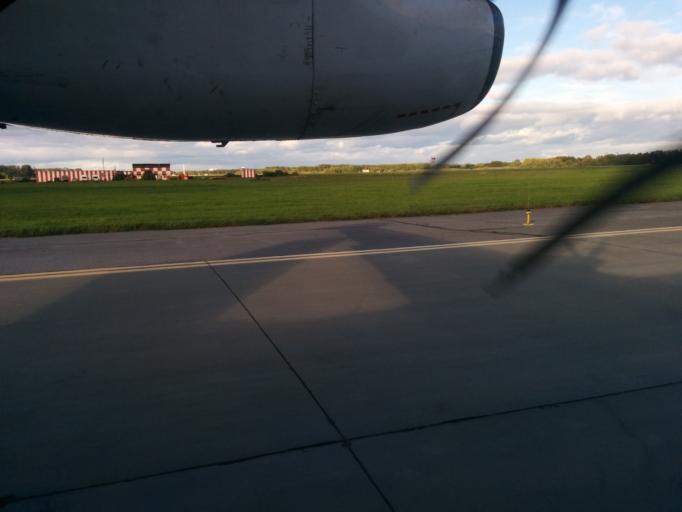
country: RU
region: Perm
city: Kultayevo
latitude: 57.9180
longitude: 56.0225
